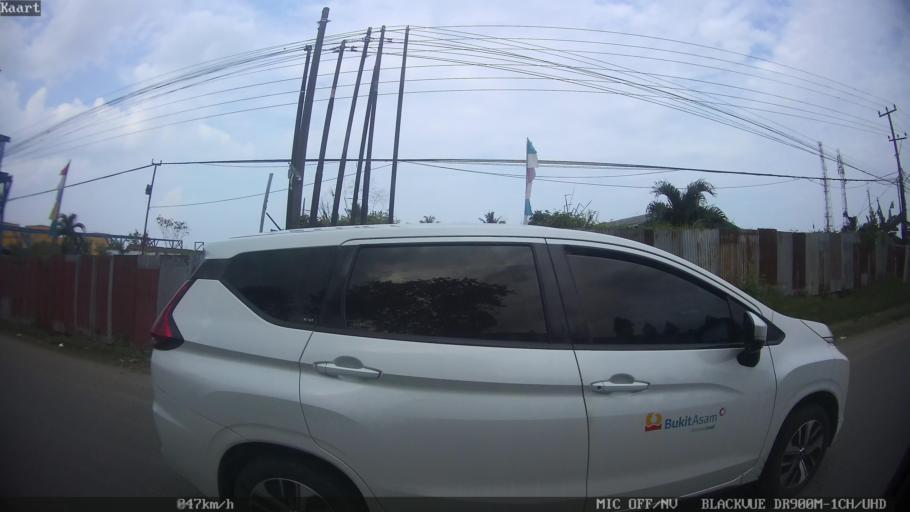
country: ID
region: Lampung
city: Panjang
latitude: -5.4560
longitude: 105.3118
